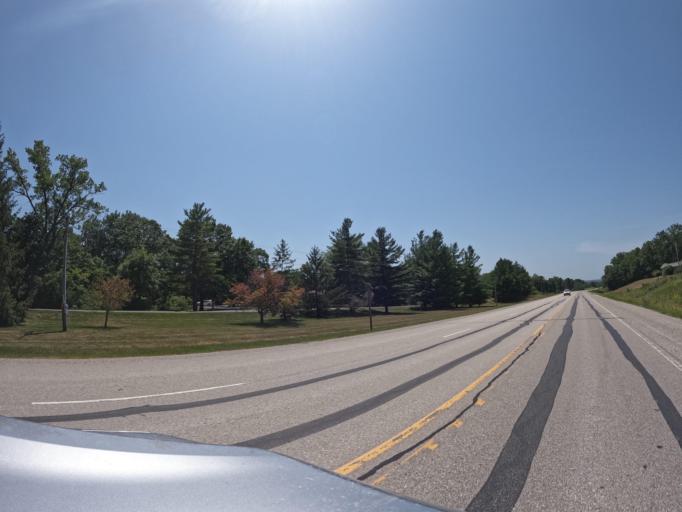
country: US
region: Iowa
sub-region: Henry County
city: Mount Pleasant
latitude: 40.9671
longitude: -91.6230
